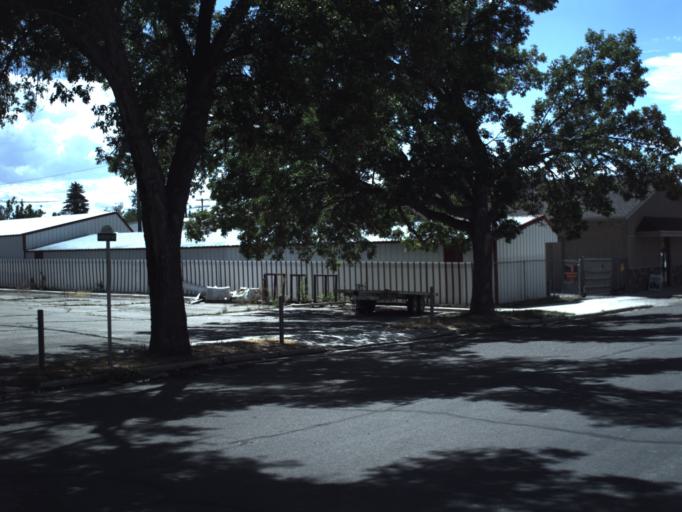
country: US
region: Utah
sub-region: Sanpete County
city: Ephraim
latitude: 39.3598
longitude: -111.5881
